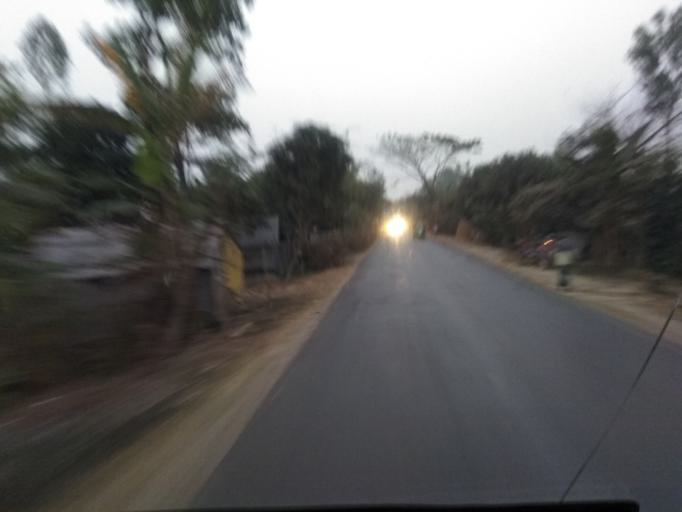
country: BD
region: Rajshahi
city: Bogra
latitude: 24.7488
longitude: 89.3411
